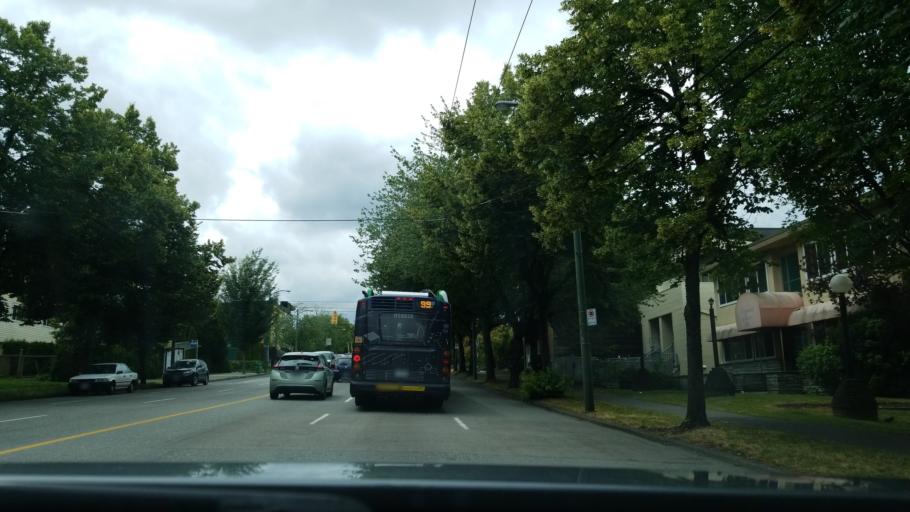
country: CA
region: British Columbia
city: Vancouver
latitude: 49.2625
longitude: -123.0840
